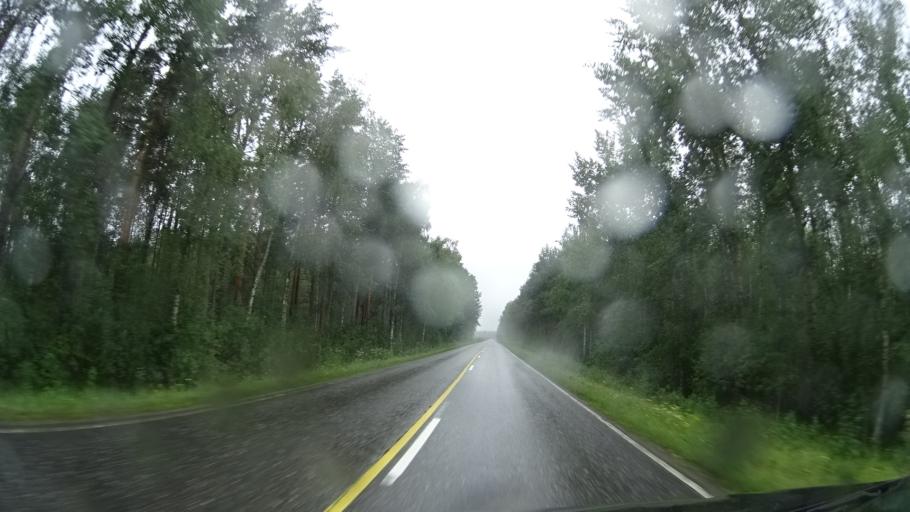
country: FI
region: North Karelia
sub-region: Keski-Karjala
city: Raeaekkylae
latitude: 62.3091
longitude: 29.5311
